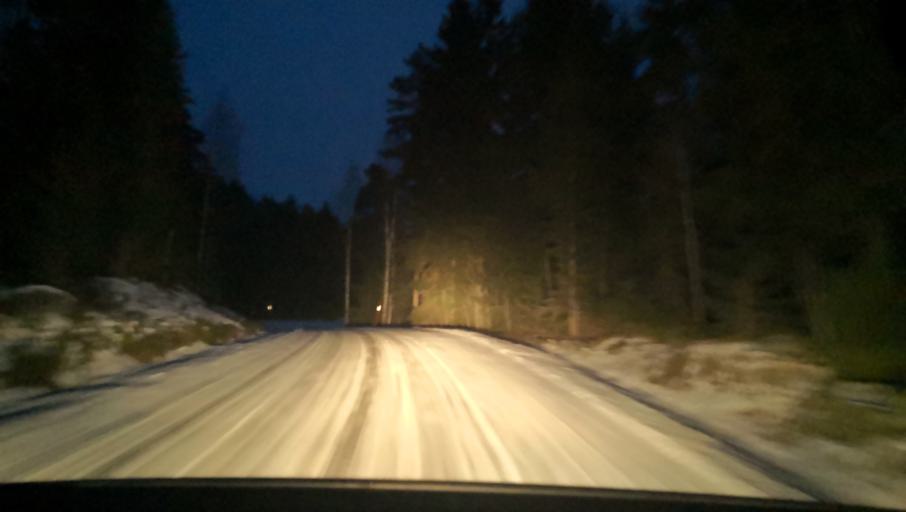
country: SE
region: Uppsala
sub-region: Heby Kommun
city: Tarnsjo
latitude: 60.2576
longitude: 16.7742
